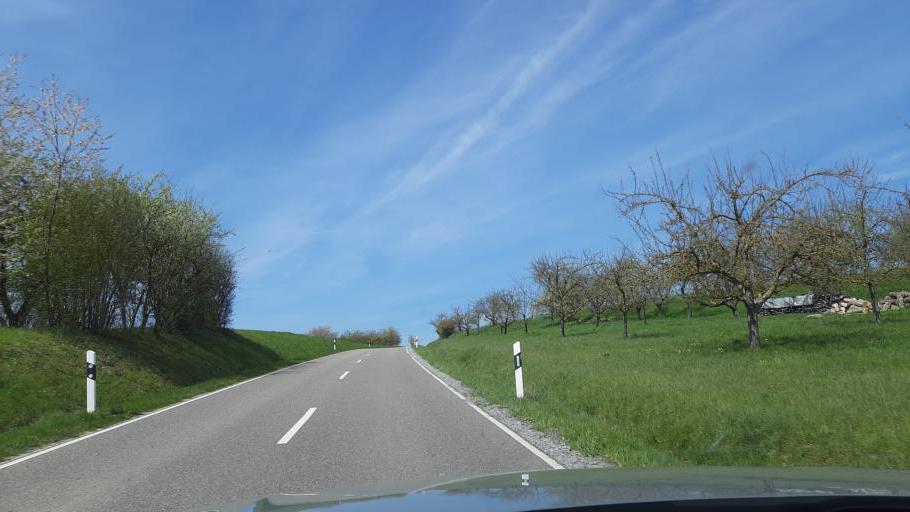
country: DE
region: Baden-Wuerttemberg
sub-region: Regierungsbezirk Stuttgart
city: Neuenstadt am Kocher
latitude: 49.2194
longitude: 9.3765
